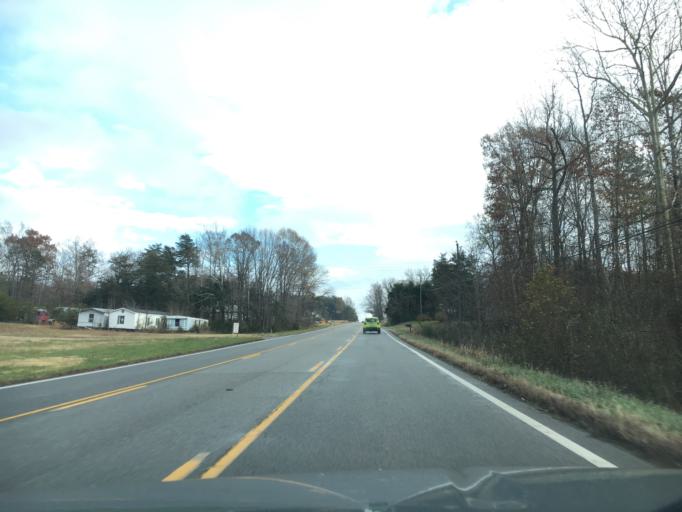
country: US
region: Virginia
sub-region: Prince Edward County
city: Farmville
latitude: 37.3158
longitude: -78.4461
